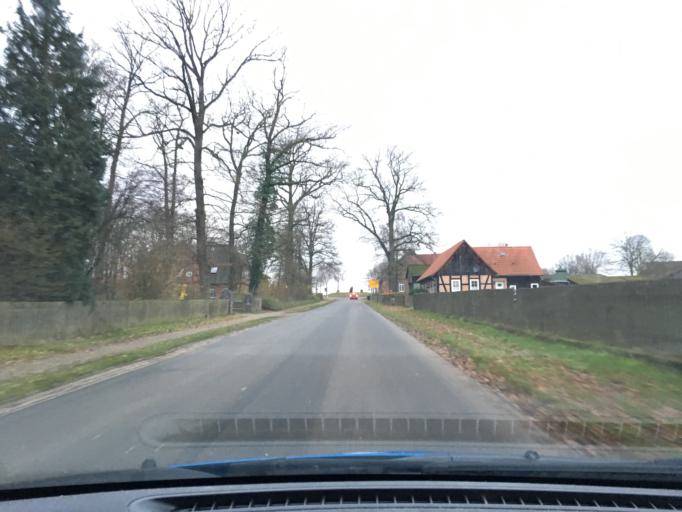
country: DE
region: Lower Saxony
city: Hermannsburg
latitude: 52.8460
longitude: 10.0773
